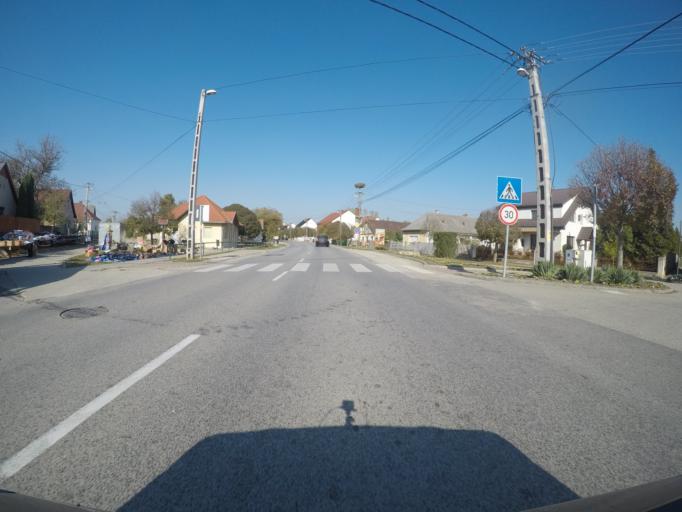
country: HU
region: Tolna
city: Nagydorog
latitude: 46.6223
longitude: 18.6561
